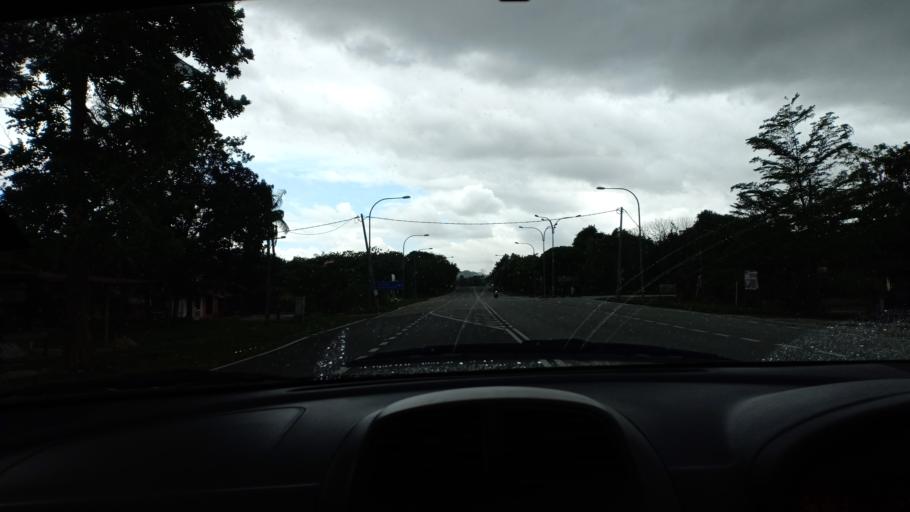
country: MY
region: Penang
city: Tasek Glugor
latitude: 5.4419
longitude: 100.4731
